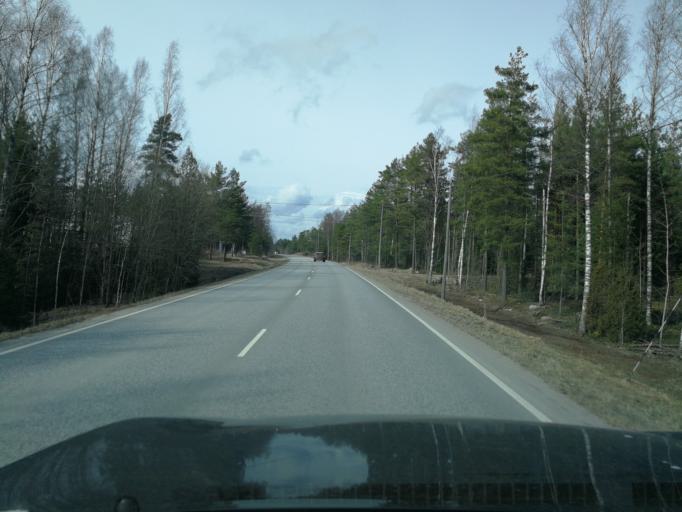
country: FI
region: Uusimaa
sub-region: Helsinki
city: Siuntio
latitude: 60.0995
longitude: 24.2510
